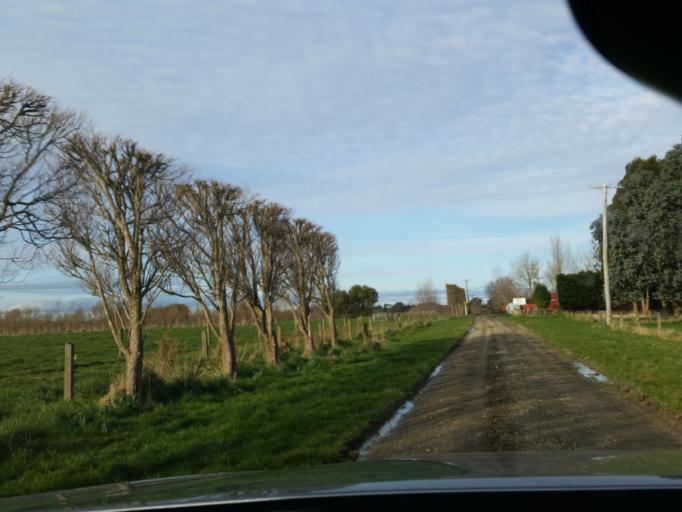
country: NZ
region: Southland
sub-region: Invercargill City
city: Invercargill
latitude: -46.3217
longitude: 168.3079
